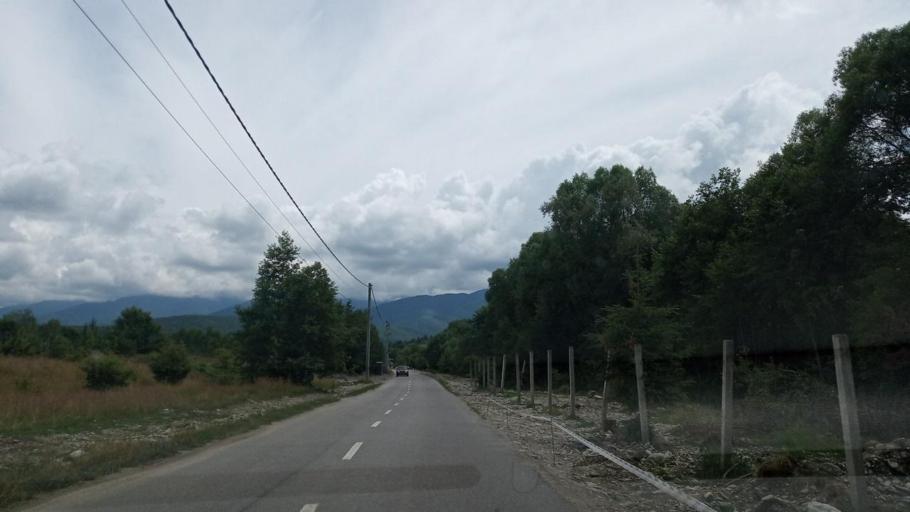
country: RO
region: Sibiu
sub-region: Comuna Porumbacu de Jos
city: Porumbacu de Jos
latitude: 45.6971
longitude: 24.4923
